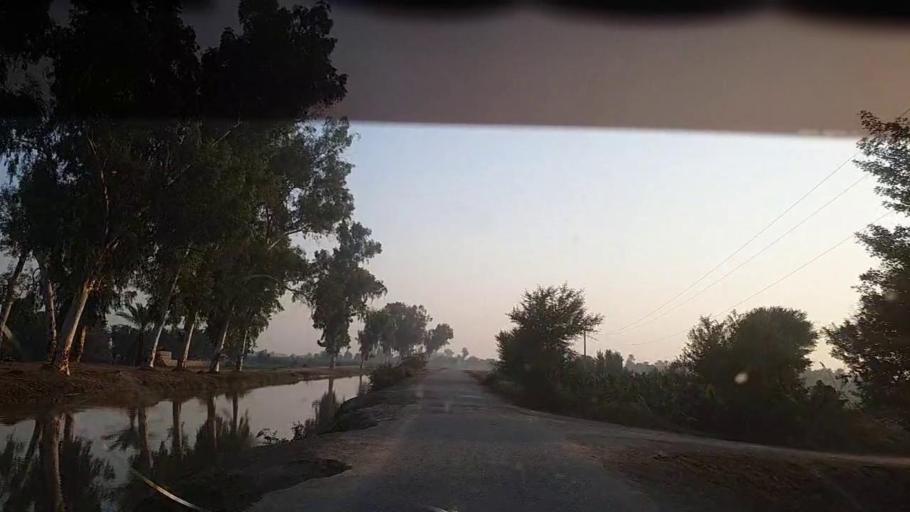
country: PK
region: Sindh
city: Ranipur
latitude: 27.2374
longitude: 68.5494
